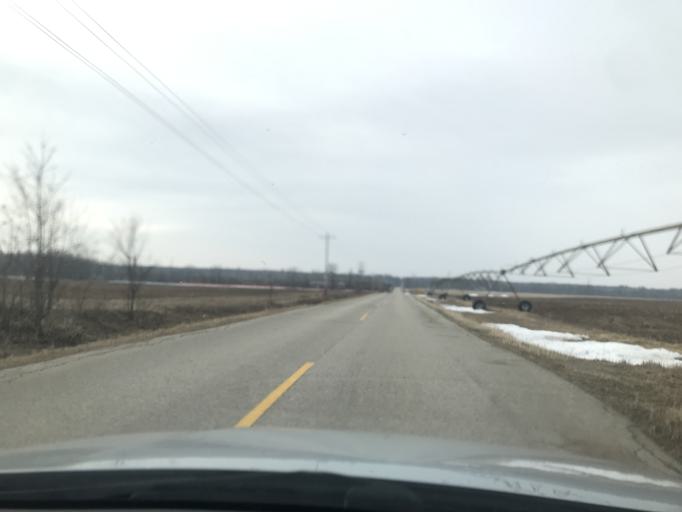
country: US
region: Wisconsin
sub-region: Oconto County
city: Oconto Falls
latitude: 44.8475
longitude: -88.1677
